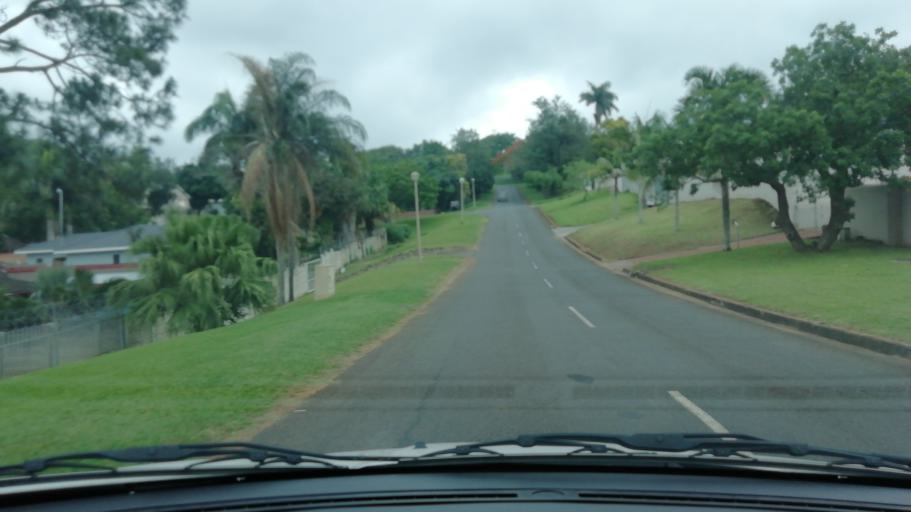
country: ZA
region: KwaZulu-Natal
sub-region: uThungulu District Municipality
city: Empangeni
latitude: -28.7570
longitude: 31.8857
